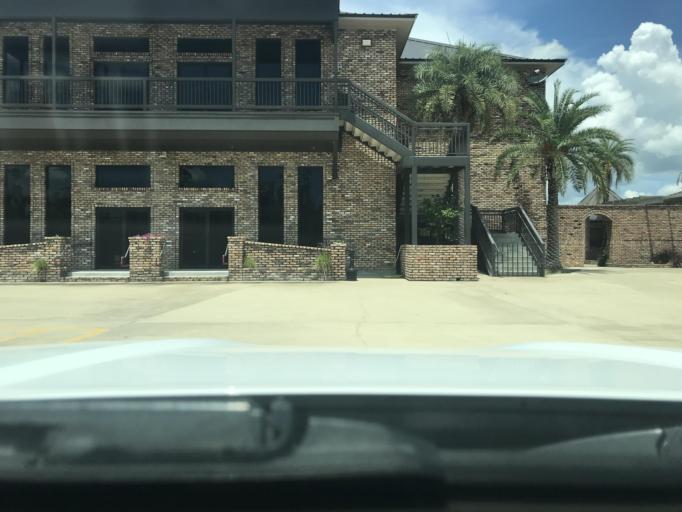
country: US
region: Louisiana
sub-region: Calcasieu Parish
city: Moss Bluff
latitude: 30.2870
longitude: -93.1671
